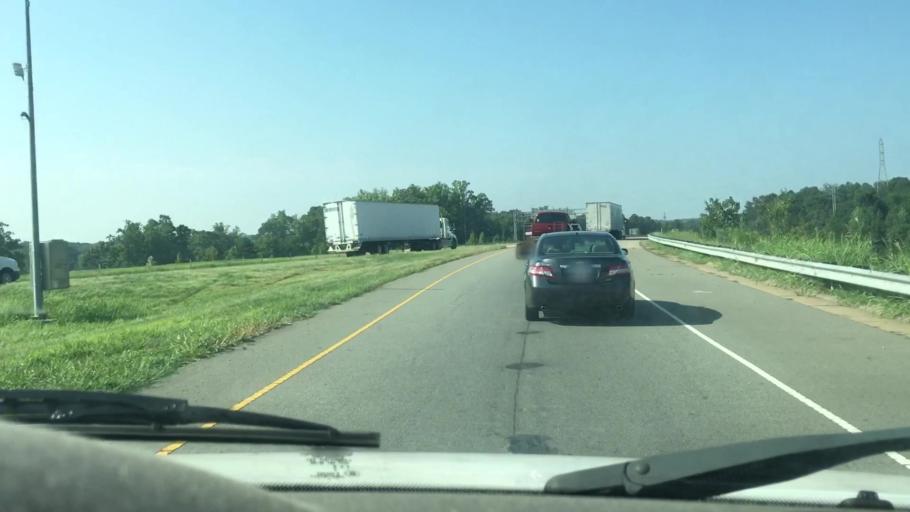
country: US
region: North Carolina
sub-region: Gaston County
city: Mount Holly
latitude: 35.3198
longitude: -80.9437
